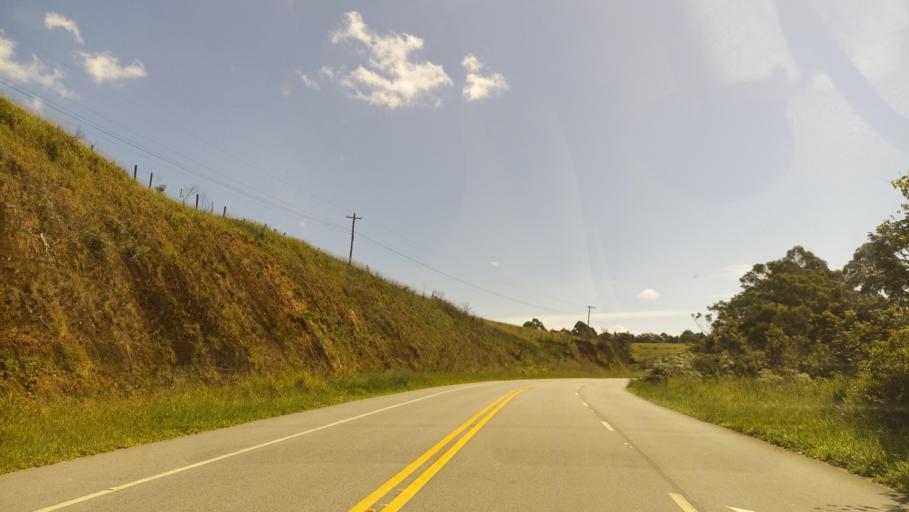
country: BR
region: Sao Paulo
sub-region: Guaratingueta
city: Guaratingueta
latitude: -22.9339
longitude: -45.0740
